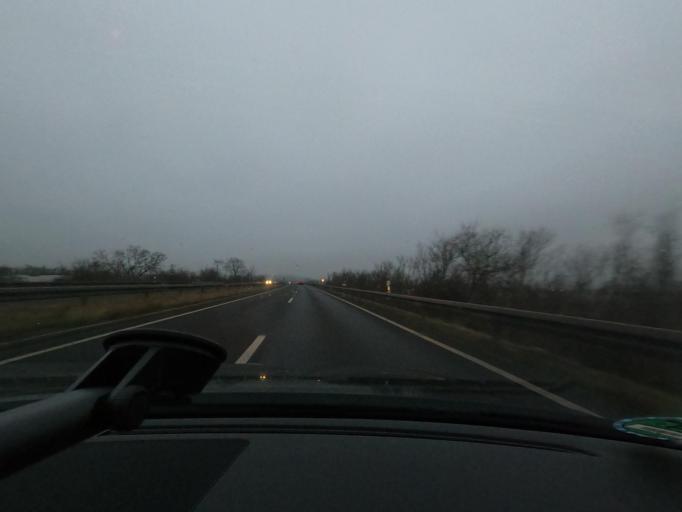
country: DE
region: Thuringia
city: Elxleben
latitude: 51.0462
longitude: 10.9379
